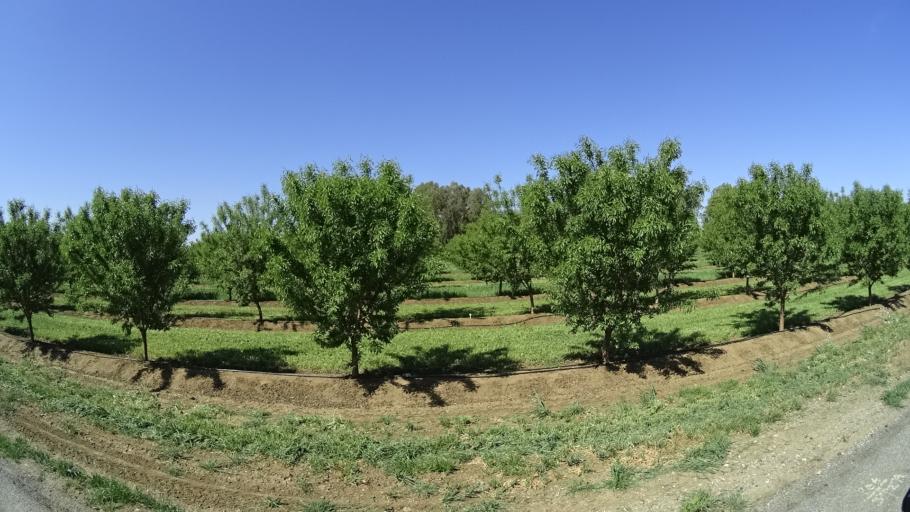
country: US
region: California
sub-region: Glenn County
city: Willows
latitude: 39.5158
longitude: -122.1864
